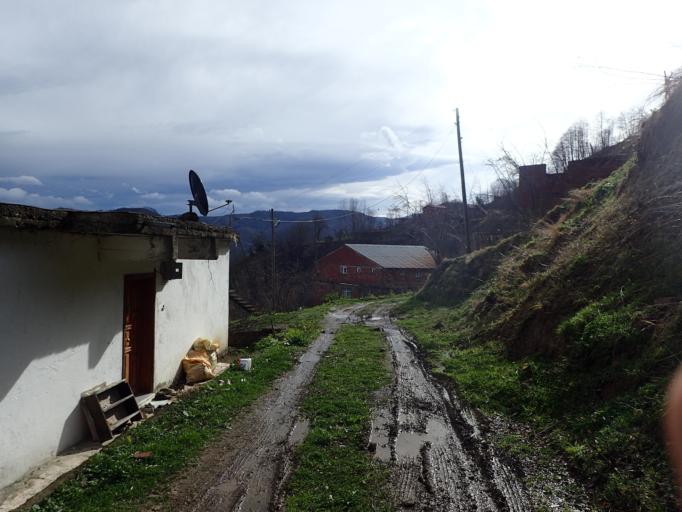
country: TR
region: Ordu
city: Camas
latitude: 40.8918
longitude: 37.5773
